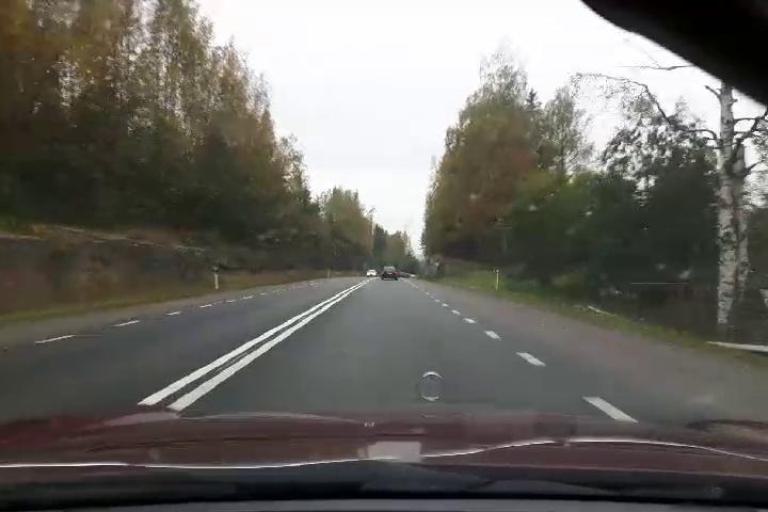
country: SE
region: Vaesternorrland
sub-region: OErnskoeldsviks Kommun
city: Ornskoldsvik
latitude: 63.2956
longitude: 18.6713
